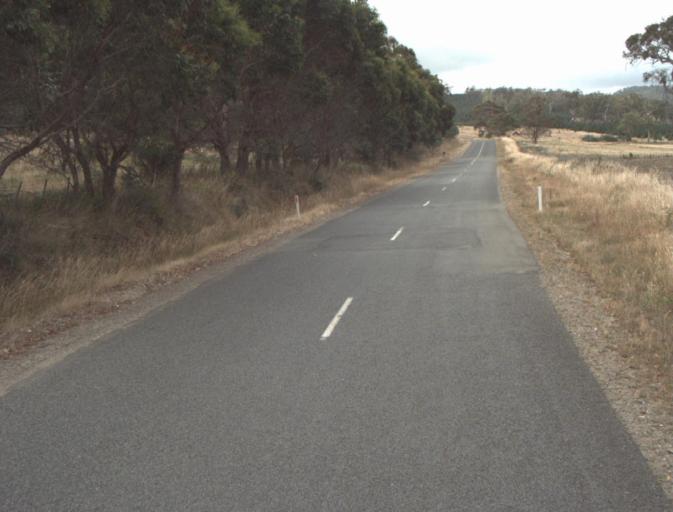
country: AU
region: Tasmania
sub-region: Northern Midlands
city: Evandale
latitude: -41.5067
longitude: 147.3752
